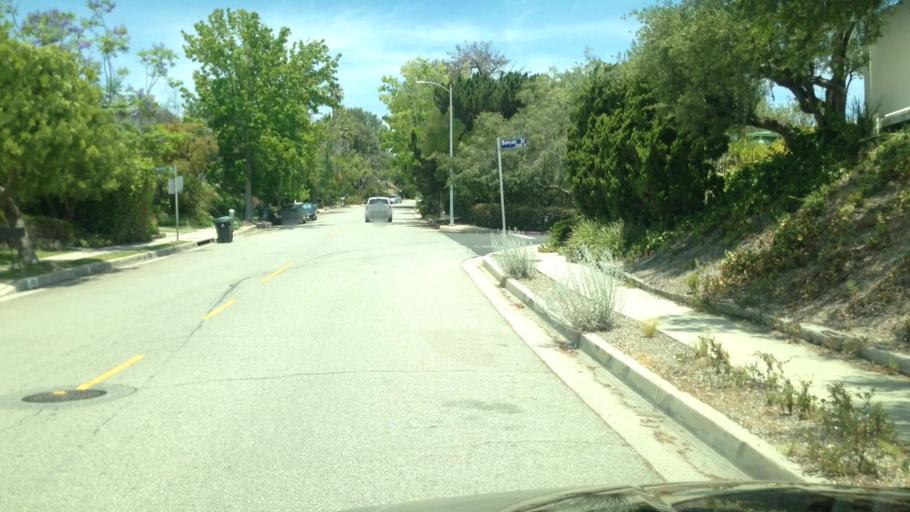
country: US
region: California
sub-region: Los Angeles County
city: Santa Monica
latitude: 34.0812
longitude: -118.5071
